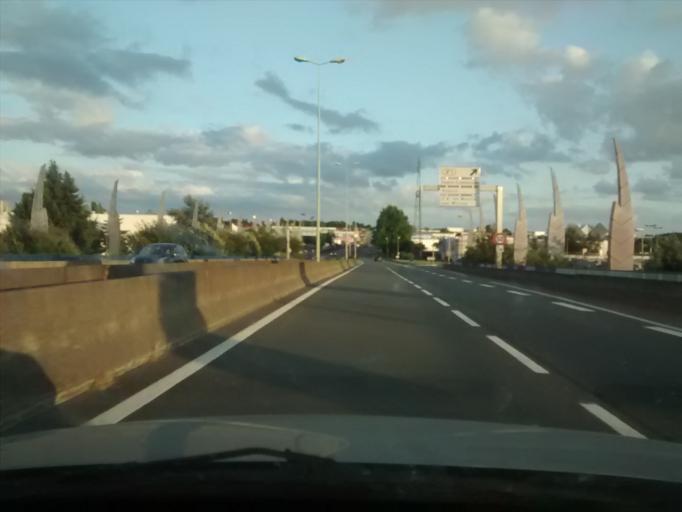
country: FR
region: Pays de la Loire
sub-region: Departement de la Sarthe
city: La Chapelle-Saint-Aubin
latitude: 48.0441
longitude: 0.1726
